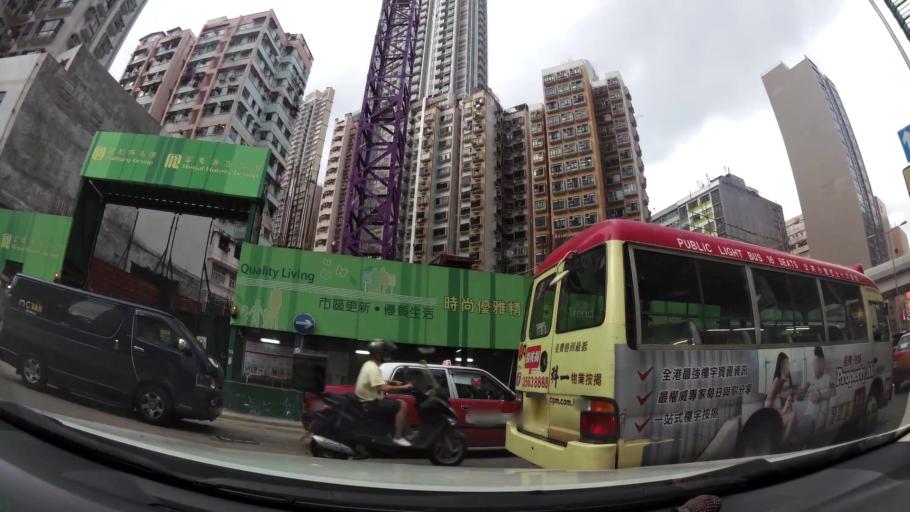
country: HK
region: Sham Shui Po
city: Sham Shui Po
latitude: 22.3200
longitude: 114.1652
